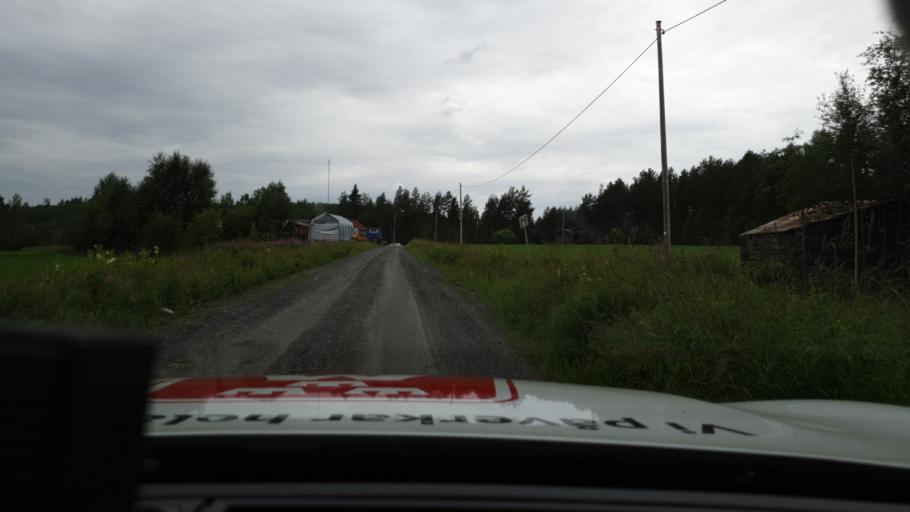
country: SE
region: Norrbotten
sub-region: Bodens Kommun
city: Boden
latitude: 65.9603
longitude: 21.8150
